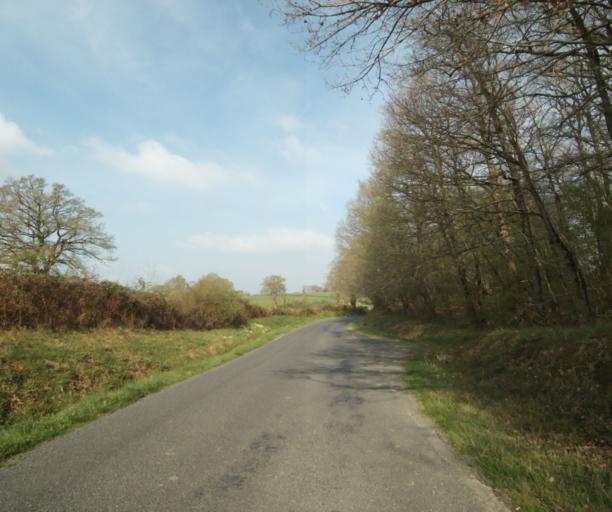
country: FR
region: Bourgogne
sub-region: Departement de Saone-et-Loire
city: Paray-le-Monial
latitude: 46.4278
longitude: 4.1795
